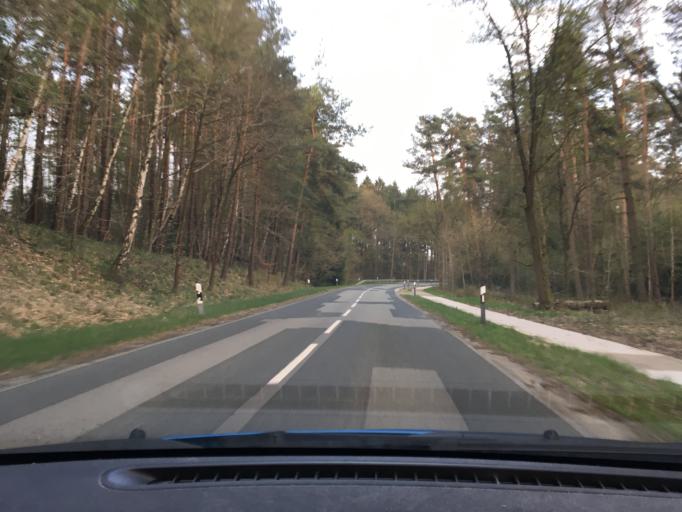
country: DE
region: Lower Saxony
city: Oldendorf
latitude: 53.1657
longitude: 10.2466
